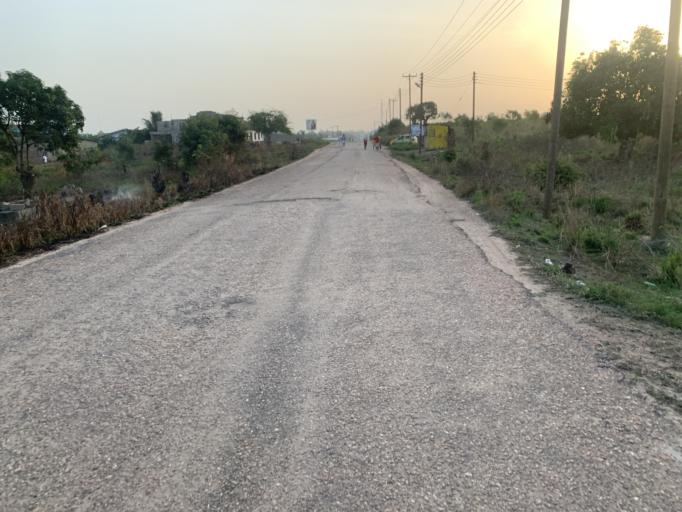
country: GH
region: Central
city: Winneba
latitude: 5.3587
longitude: -0.6068
